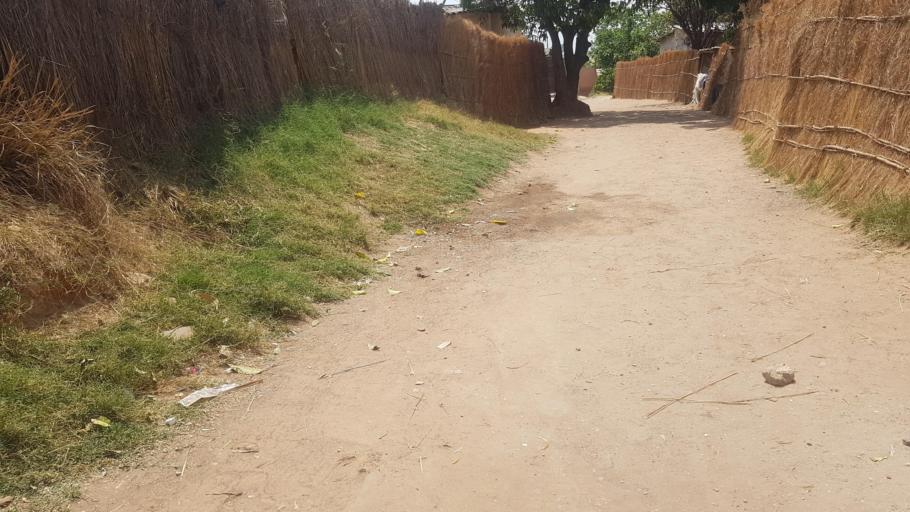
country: ZM
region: Lusaka
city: Lusaka
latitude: -15.4408
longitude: 28.3846
